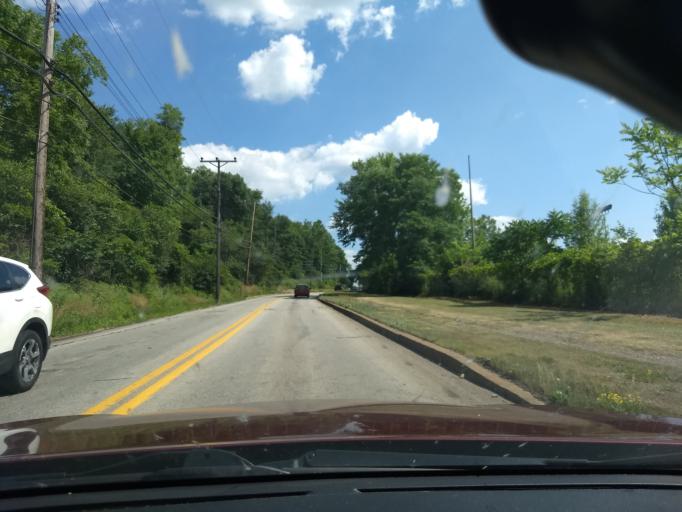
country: US
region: Pennsylvania
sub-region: Westmoreland County
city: Trafford
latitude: 40.3949
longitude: -79.7671
